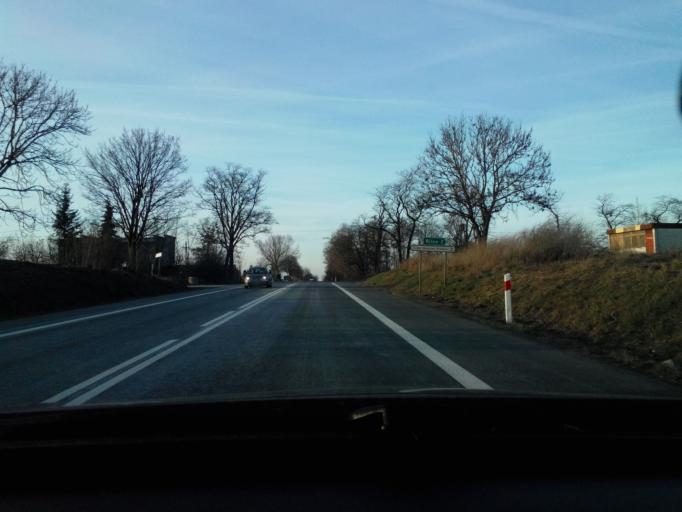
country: PL
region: Kujawsko-Pomorskie
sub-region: Powiat wloclawski
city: Lubien Kujawski
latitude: 52.4463
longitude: 19.1599
